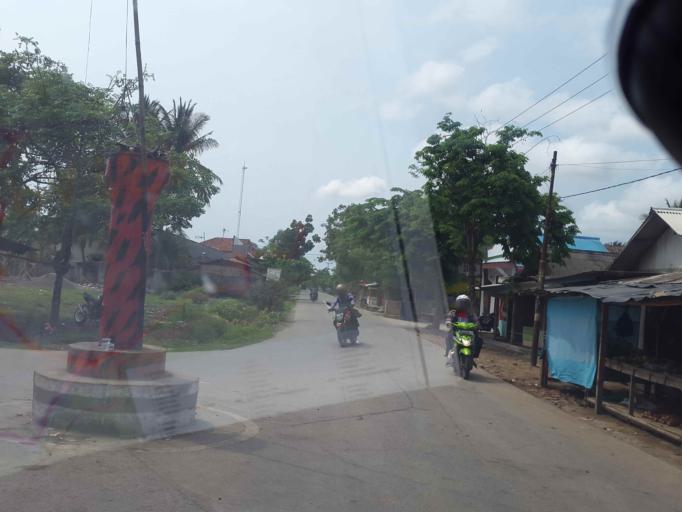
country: ID
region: West Java
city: Rengasdengklok
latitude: -6.0907
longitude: 107.1849
